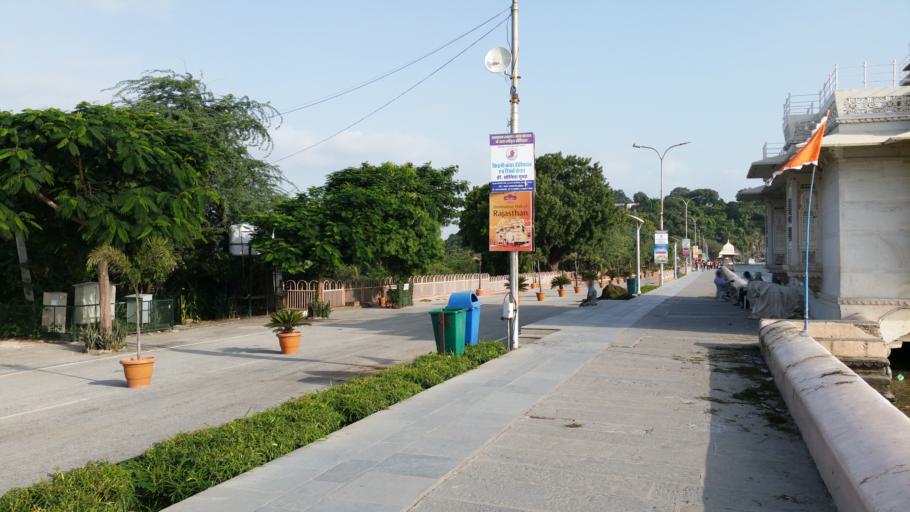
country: IN
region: Rajasthan
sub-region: Udaipur
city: Udaipur
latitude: 24.6052
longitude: 73.6786
